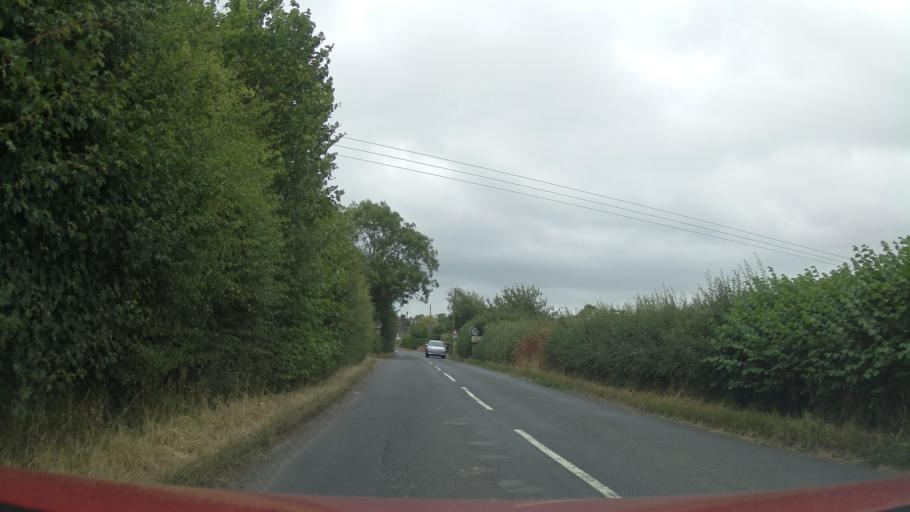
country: GB
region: England
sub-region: Derbyshire
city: Swadlincote
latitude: 52.7887
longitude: -1.5311
